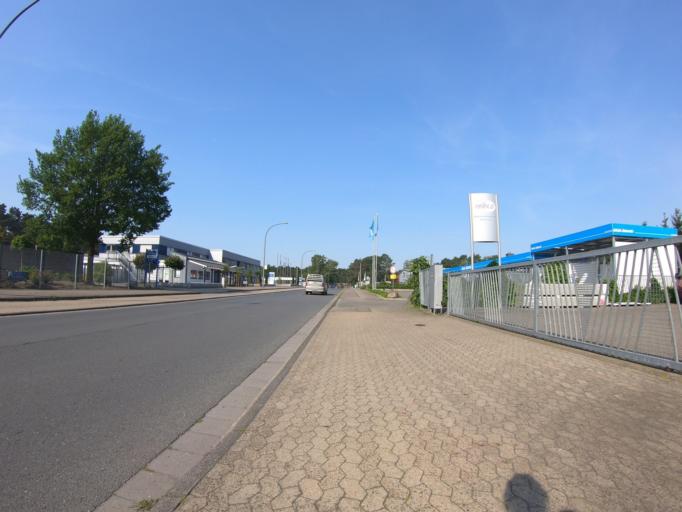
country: DE
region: Lower Saxony
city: Gifhorn
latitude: 52.4645
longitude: 10.5299
